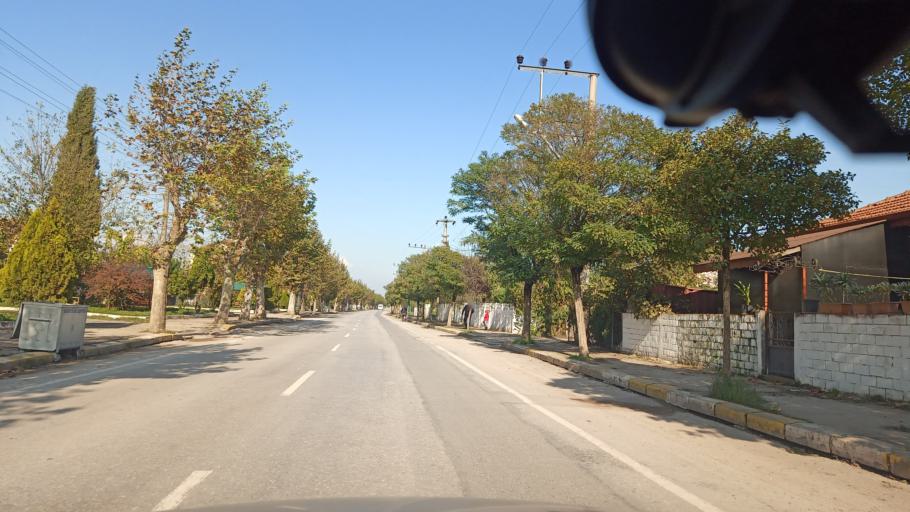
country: TR
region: Sakarya
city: Sogutlu
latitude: 40.8831
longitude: 30.4637
